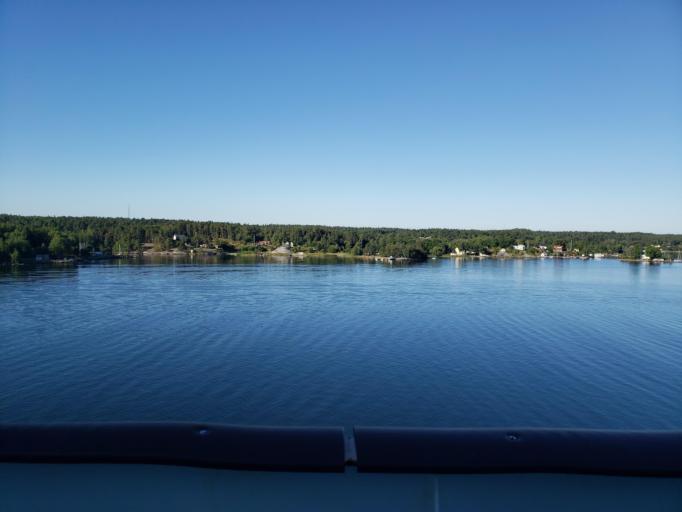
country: SE
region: Stockholm
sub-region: Vaxholms Kommun
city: Vaxholm
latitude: 59.4056
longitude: 18.4276
